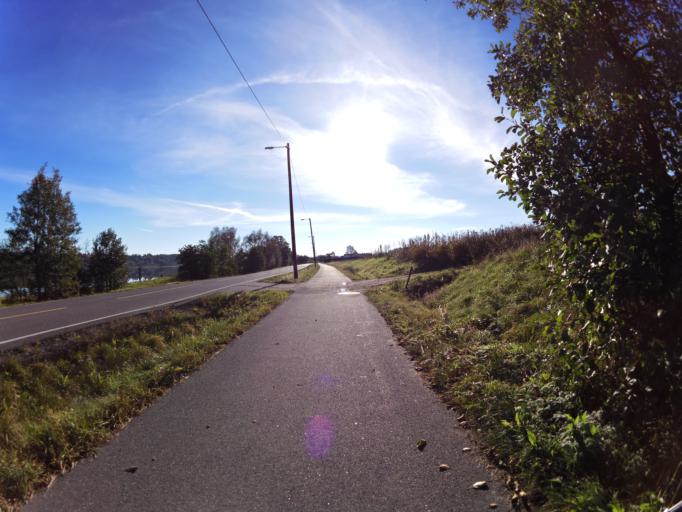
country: NO
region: Ostfold
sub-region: Fredrikstad
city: Fredrikstad
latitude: 59.2859
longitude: 11.0063
